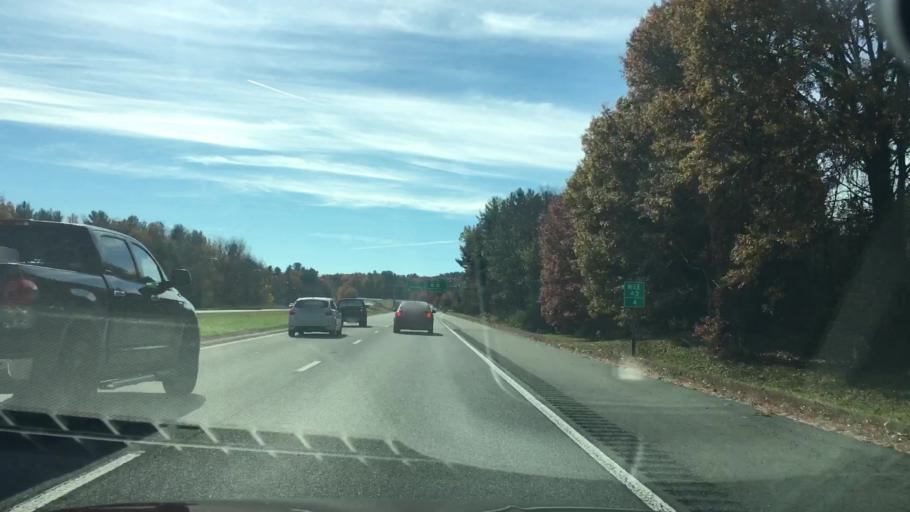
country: US
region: Massachusetts
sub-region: Franklin County
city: Greenfield
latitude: 42.5907
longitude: -72.6198
